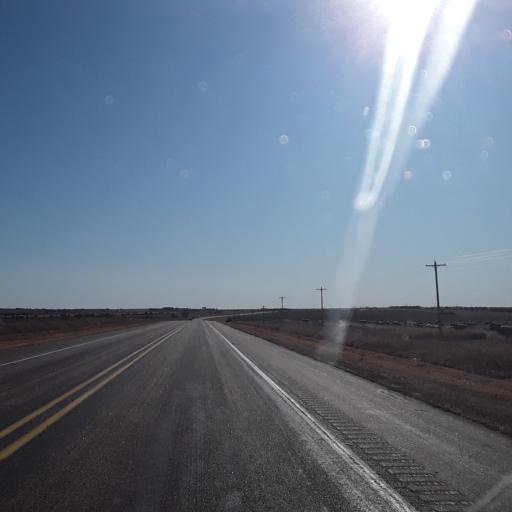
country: US
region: Nebraska
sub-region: Frontier County
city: Stockville
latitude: 40.5749
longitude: -100.6298
